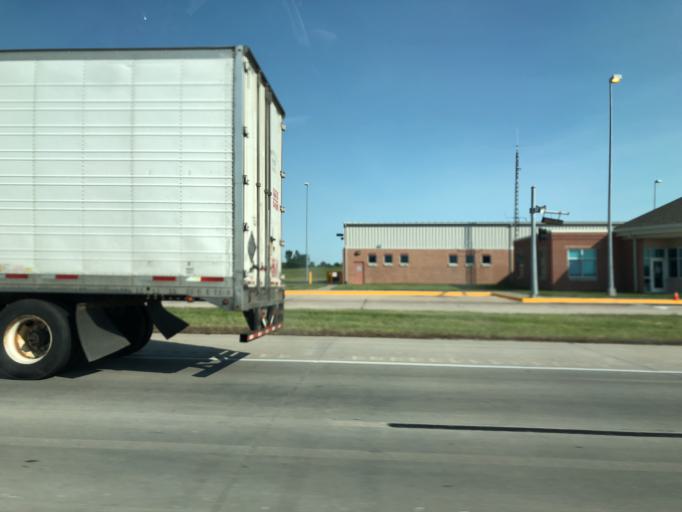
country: US
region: Nebraska
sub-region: Lancaster County
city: Waverly
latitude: 40.9225
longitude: -96.4612
